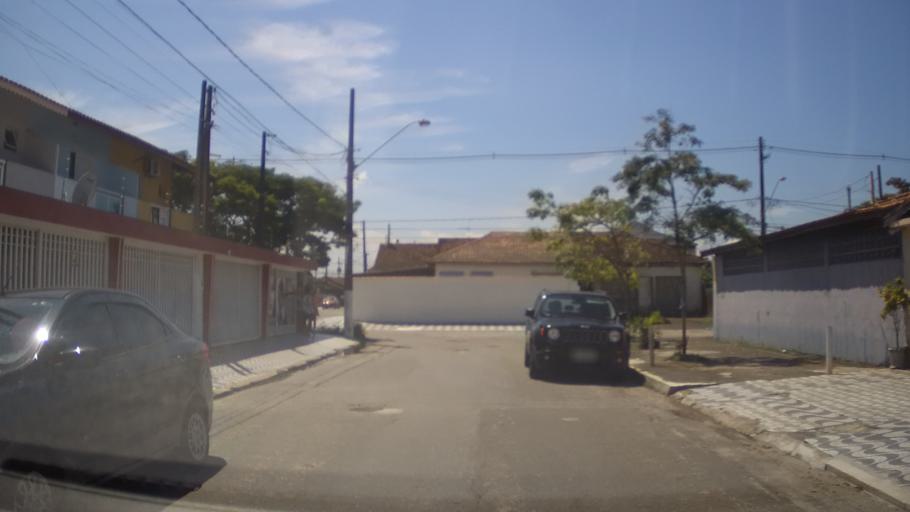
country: BR
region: Sao Paulo
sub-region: Praia Grande
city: Praia Grande
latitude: -24.0221
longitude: -46.4764
